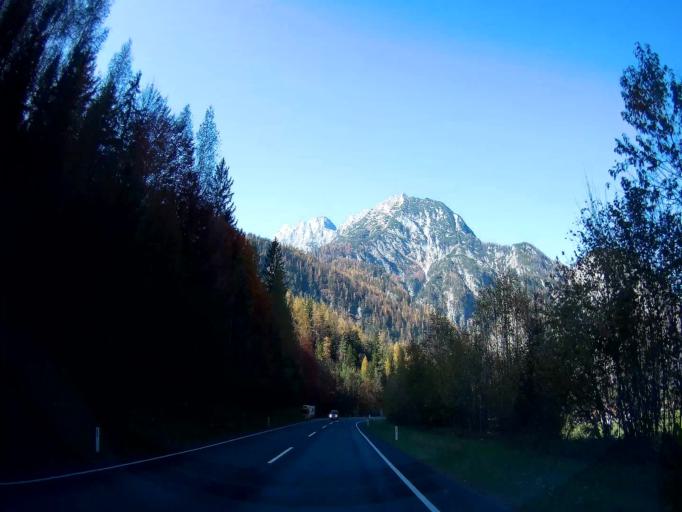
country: AT
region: Salzburg
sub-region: Politischer Bezirk Zell am See
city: Sankt Martin bei Lofer
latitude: 47.5326
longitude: 12.7287
